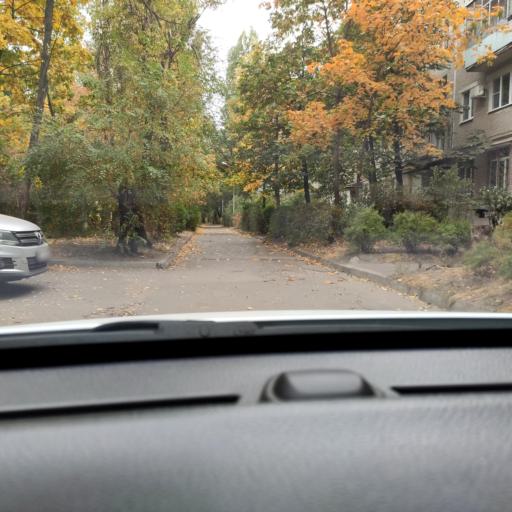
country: RU
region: Voronezj
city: Voronezh
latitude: 51.7169
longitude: 39.2700
